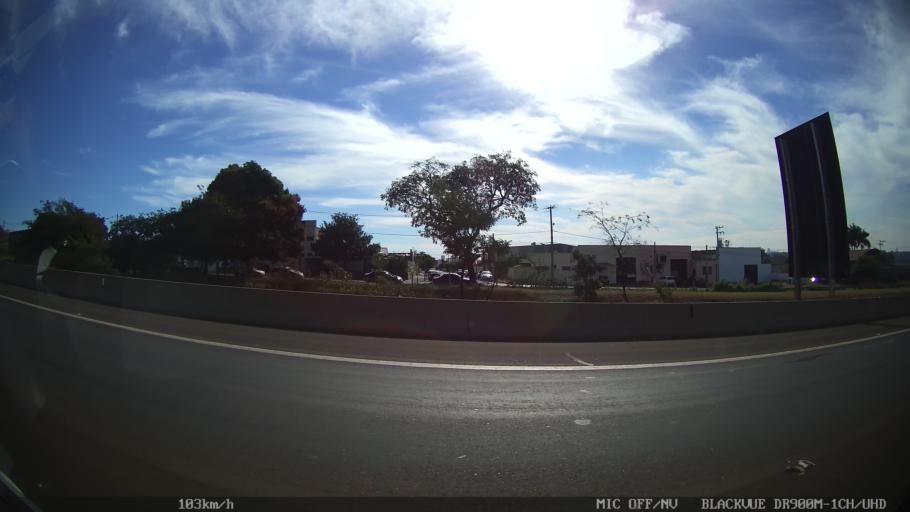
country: BR
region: Sao Paulo
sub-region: Araraquara
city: Araraquara
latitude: -21.8096
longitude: -48.1540
